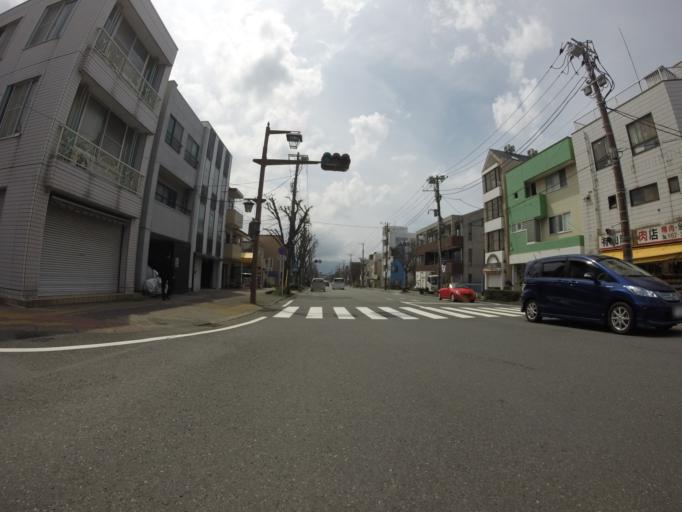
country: JP
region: Shizuoka
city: Numazu
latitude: 35.0940
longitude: 138.8573
